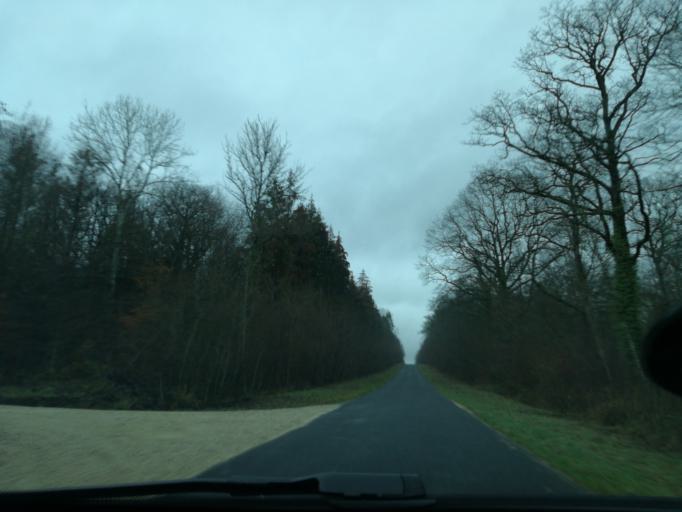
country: FR
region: Lorraine
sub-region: Departement de la Meuse
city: Revigny-sur-Ornain
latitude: 48.8560
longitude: 5.0656
